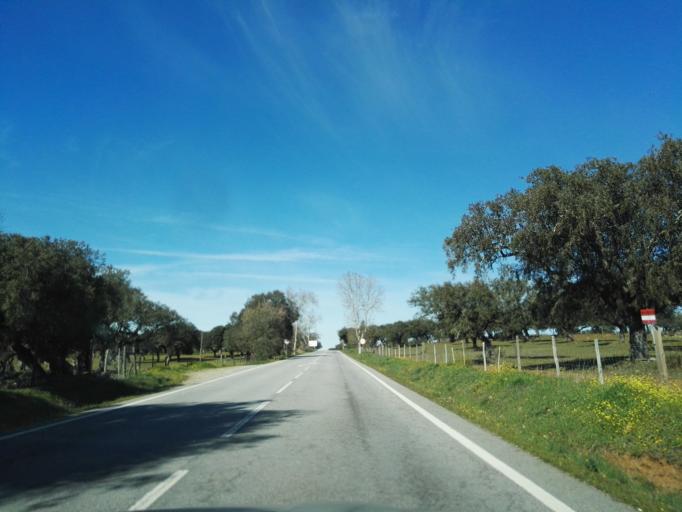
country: PT
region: Portalegre
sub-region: Arronches
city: Arronches
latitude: 39.1080
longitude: -7.2799
